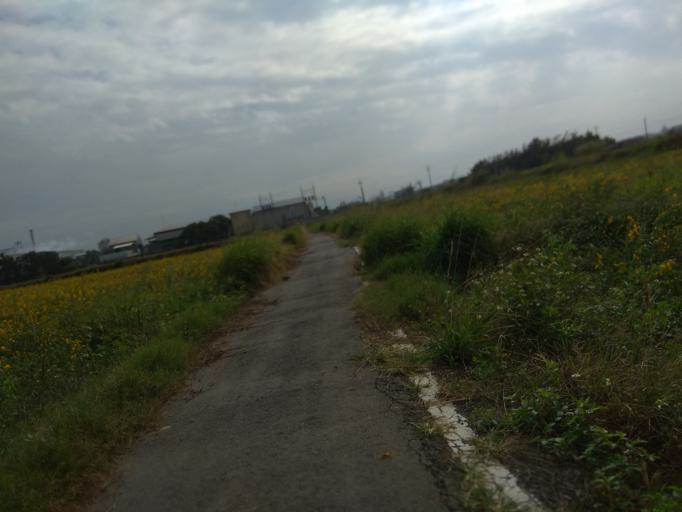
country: TW
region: Taiwan
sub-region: Hsinchu
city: Zhubei
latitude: 24.9801
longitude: 121.0345
